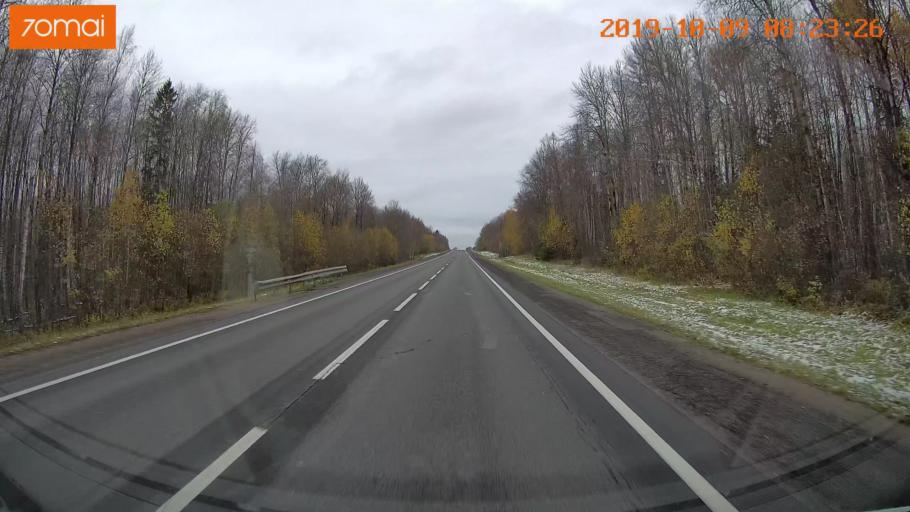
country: RU
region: Vologda
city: Gryazovets
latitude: 58.7543
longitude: 40.2834
